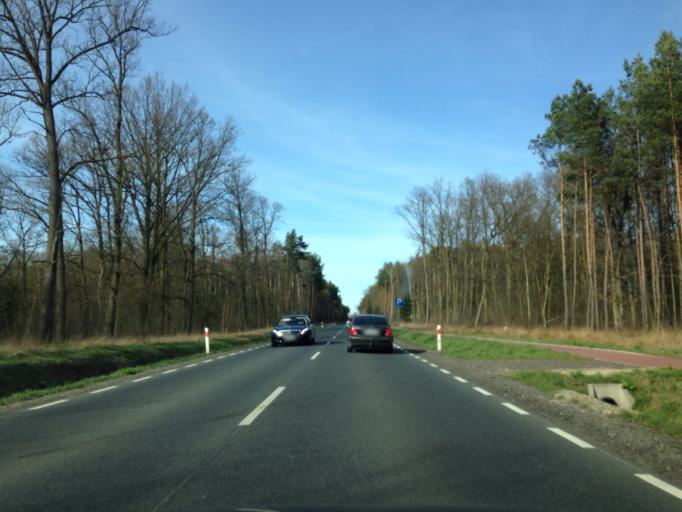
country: PL
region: Lodz Voivodeship
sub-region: Powiat poddebicki
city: Wartkowice
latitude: 51.9564
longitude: 19.0065
